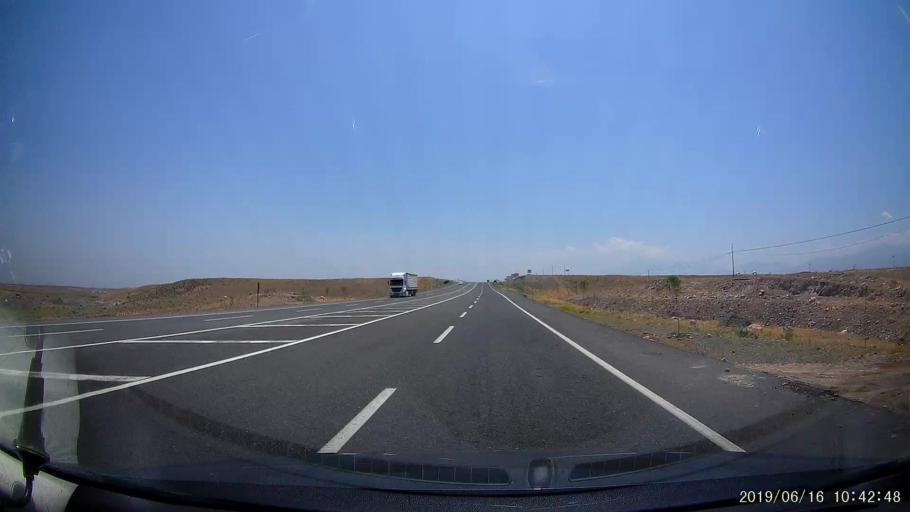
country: AM
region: Armavir
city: Shenavan
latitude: 40.0394
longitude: 43.8152
